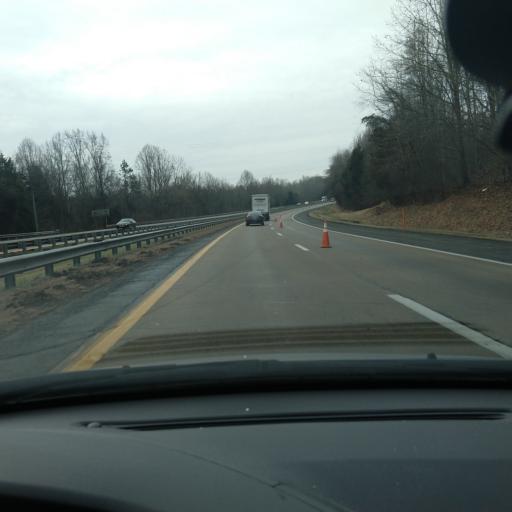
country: US
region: North Carolina
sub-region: Forsyth County
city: Winston-Salem
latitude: 36.0295
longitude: -80.2367
